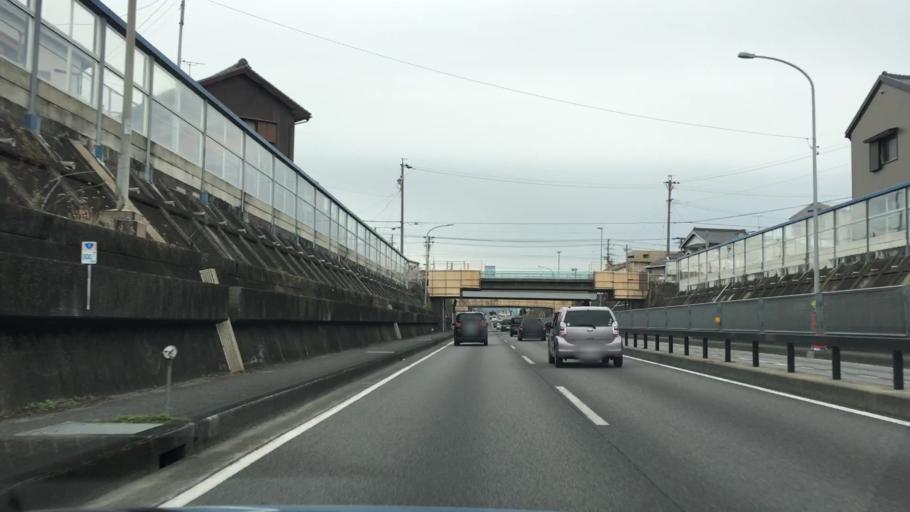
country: JP
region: Aichi
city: Kozakai-cho
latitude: 34.7987
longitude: 137.3658
